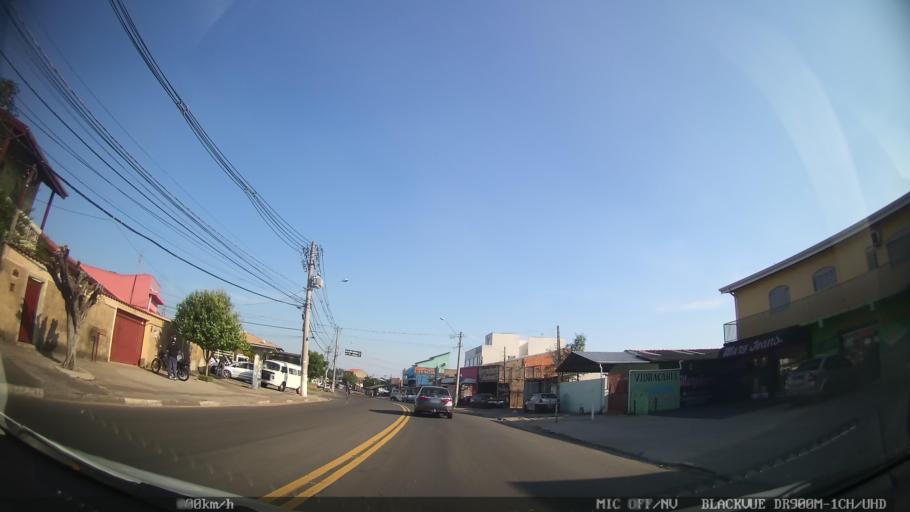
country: BR
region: Sao Paulo
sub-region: Campinas
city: Campinas
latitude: -22.9831
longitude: -47.1479
